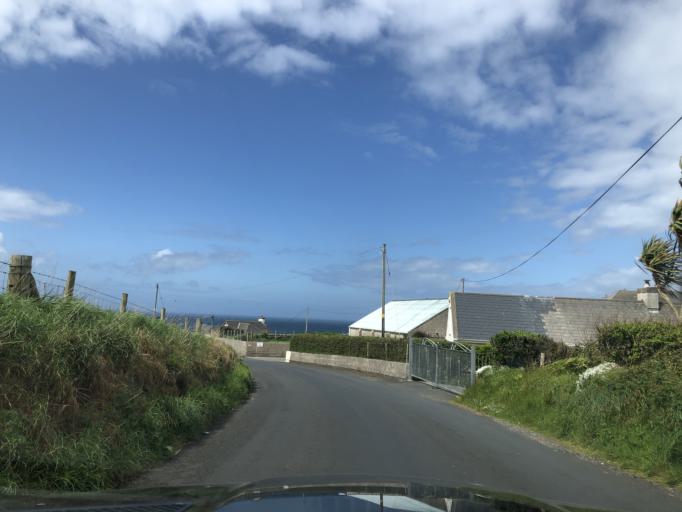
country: GB
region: Northern Ireland
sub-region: Moyle District
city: Ballycastle
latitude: 55.2420
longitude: -6.3667
